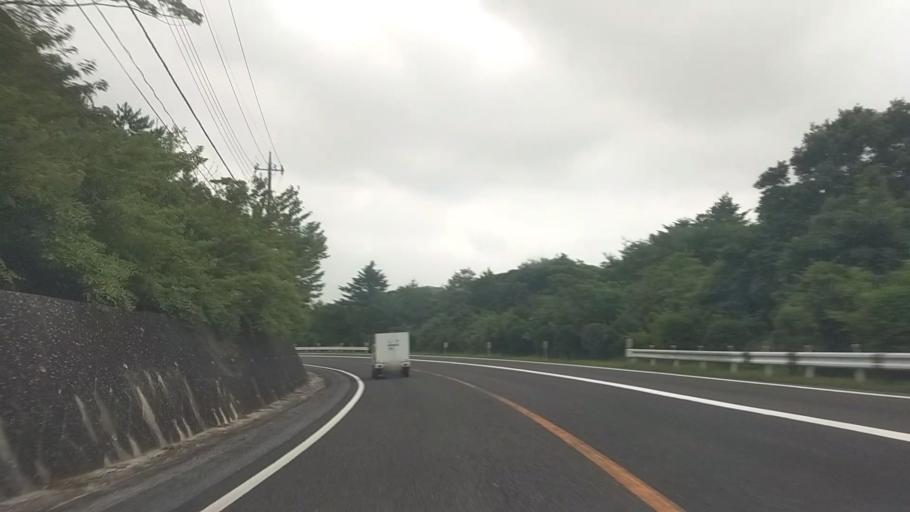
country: JP
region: Chiba
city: Kawaguchi
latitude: 35.1629
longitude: 140.0619
